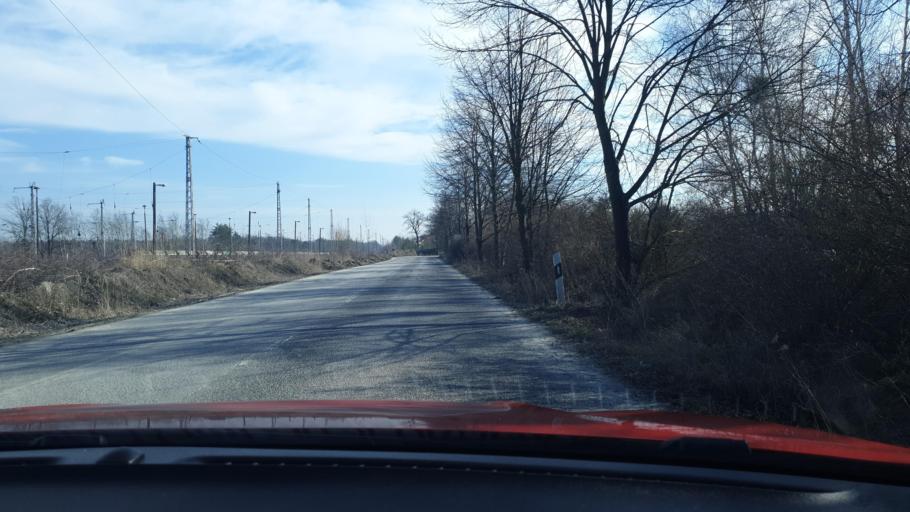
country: DE
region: Saxony
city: Ossling
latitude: 51.4421
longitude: 14.1419
